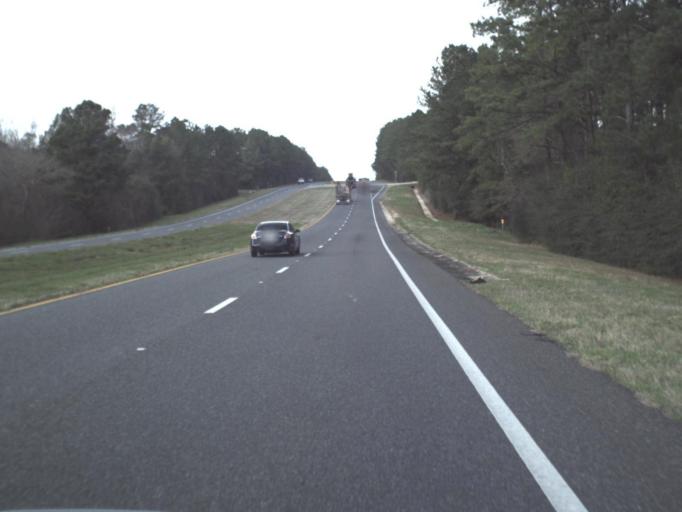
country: US
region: Florida
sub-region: Bay County
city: Youngstown
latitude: 30.5497
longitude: -85.3906
